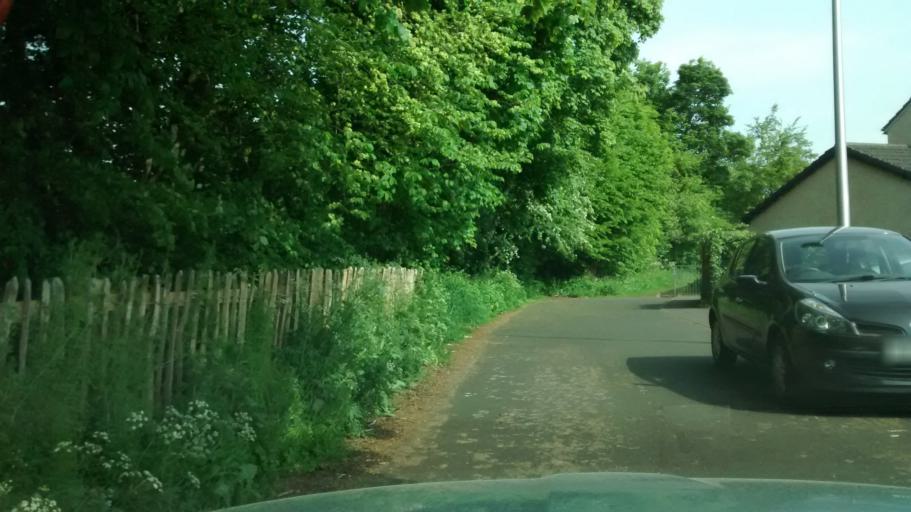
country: GB
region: Scotland
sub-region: West Lothian
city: Mid Calder
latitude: 55.8934
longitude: -3.4840
